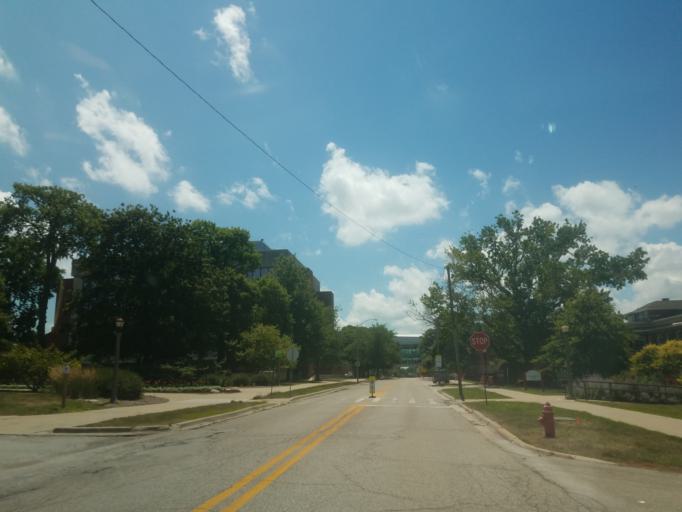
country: US
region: Illinois
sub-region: McLean County
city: Normal
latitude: 40.5099
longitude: -88.9933
